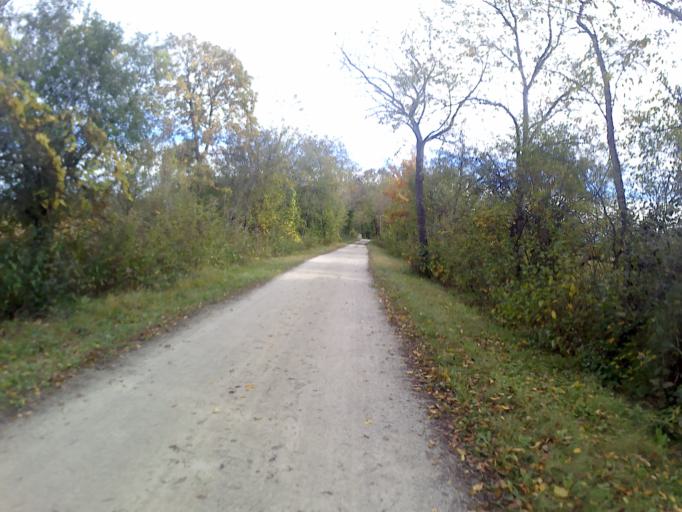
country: US
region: Illinois
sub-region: DuPage County
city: West Chicago
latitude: 41.9014
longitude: -88.1779
